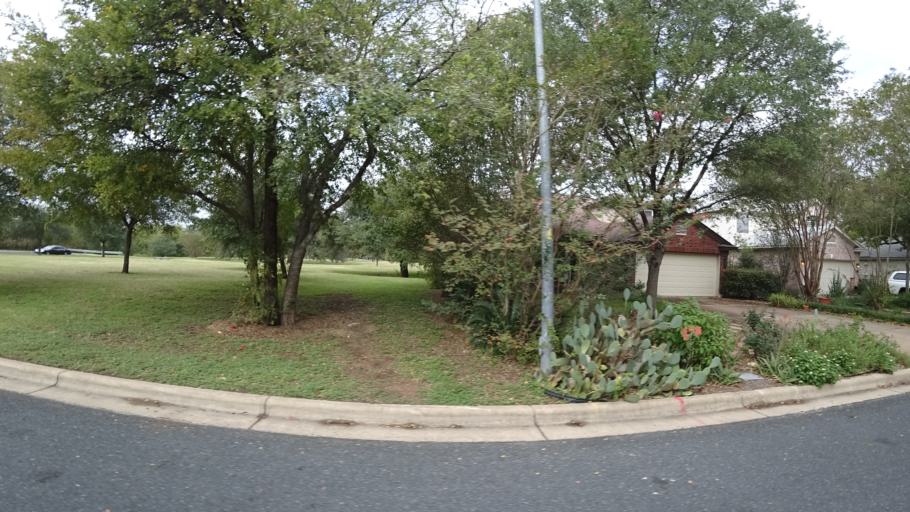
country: US
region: Texas
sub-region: Travis County
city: Shady Hollow
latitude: 30.1867
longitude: -97.8382
